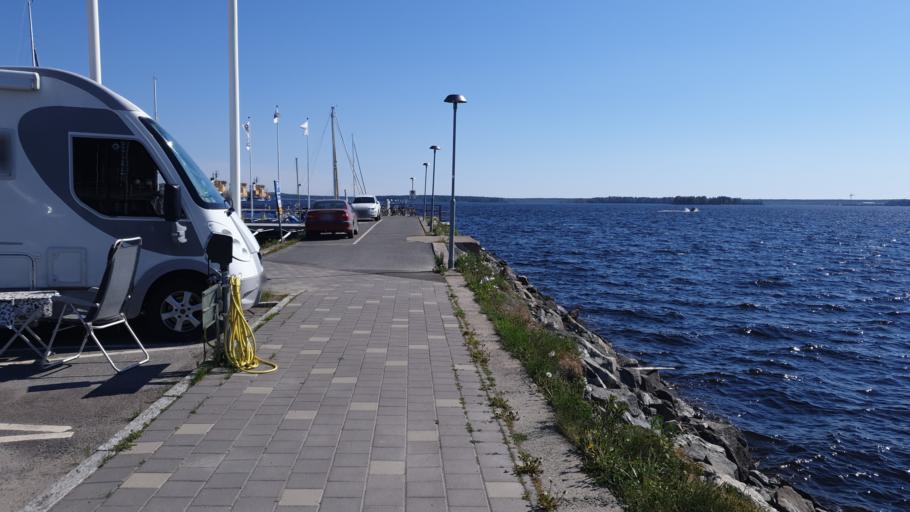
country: SE
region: Norrbotten
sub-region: Lulea Kommun
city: Lulea
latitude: 65.5801
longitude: 22.1600
